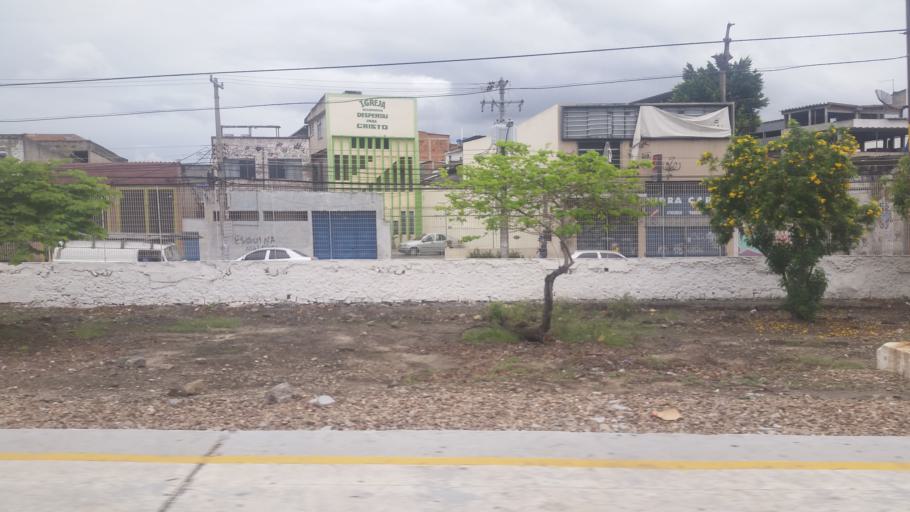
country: BR
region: Rio de Janeiro
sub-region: Sao Joao De Meriti
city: Sao Joao de Meriti
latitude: -22.8690
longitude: -43.3506
